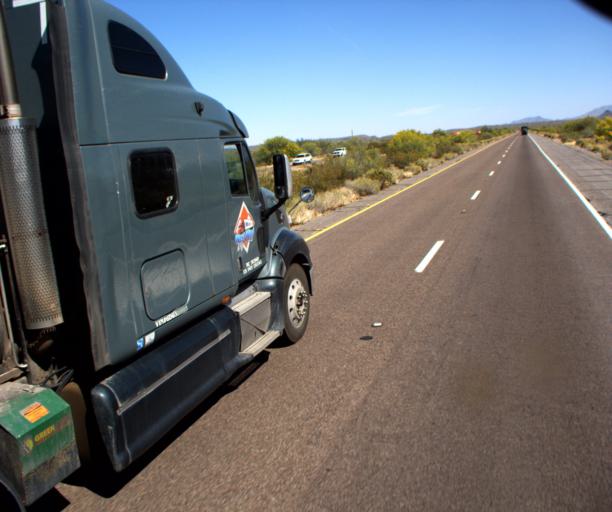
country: US
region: Arizona
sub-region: Maricopa County
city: Gila Bend
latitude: 32.8539
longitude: -112.3708
